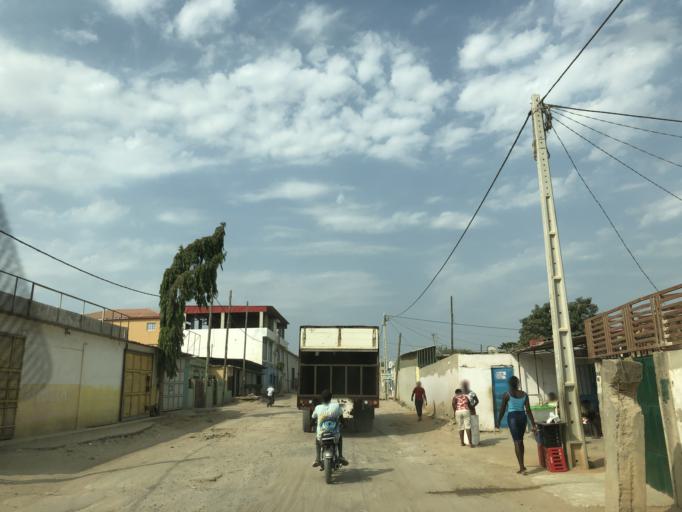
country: AO
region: Luanda
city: Luanda
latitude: -8.8999
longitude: 13.3493
